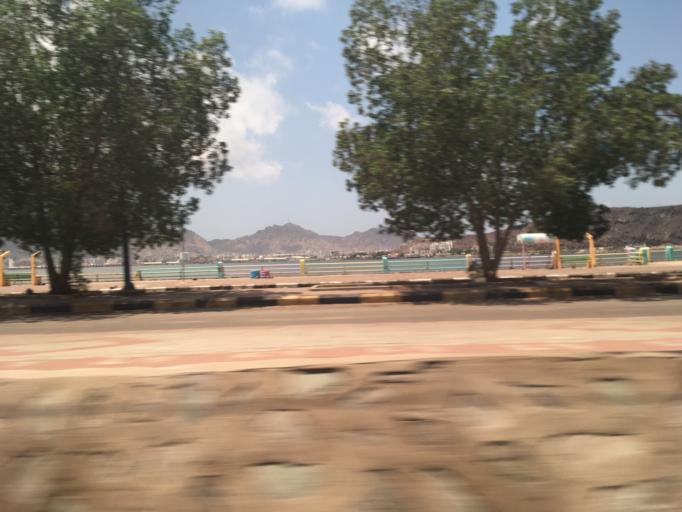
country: YE
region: Aden
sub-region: Khur Maksar
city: Khawr Maksar
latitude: 12.8083
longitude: 45.0258
